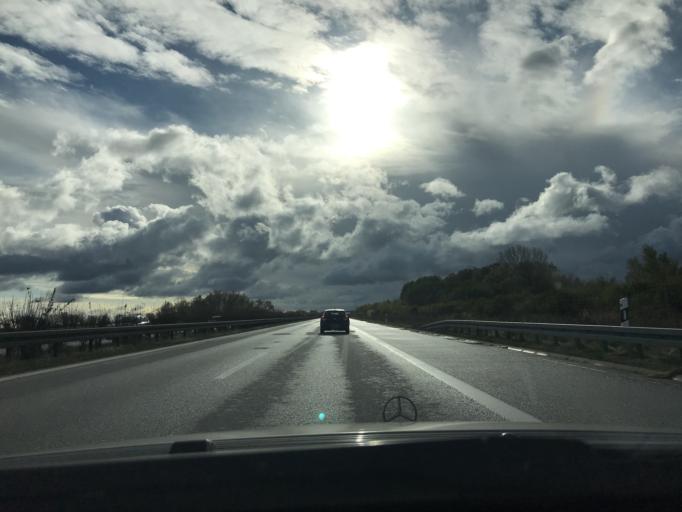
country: DE
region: Mecklenburg-Vorpommern
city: Kessin
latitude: 53.7787
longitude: 13.3280
